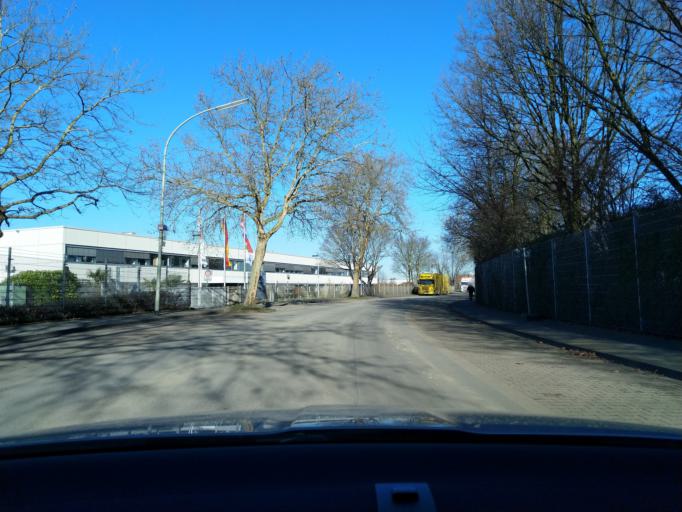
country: DE
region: North Rhine-Westphalia
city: Wegberg
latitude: 51.1474
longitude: 6.3526
